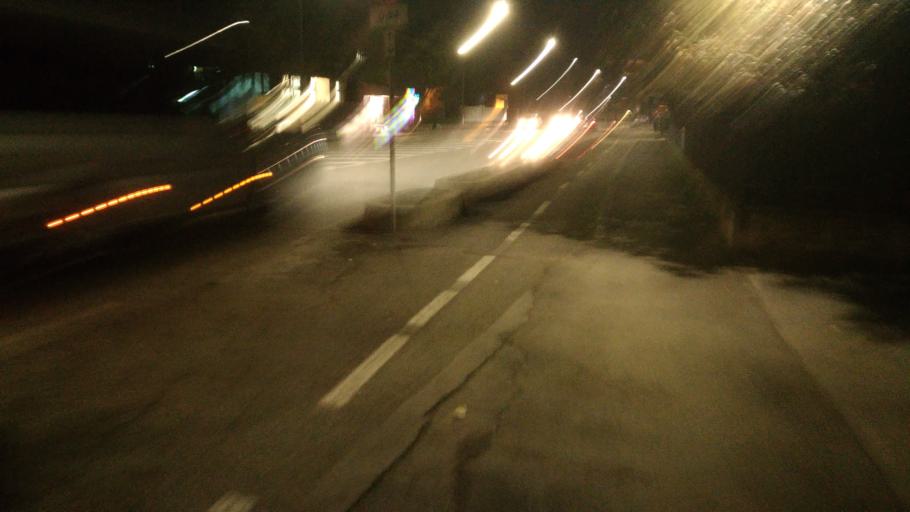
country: IT
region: Emilia-Romagna
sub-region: Provincia di Bologna
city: Trebbo
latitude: 44.5314
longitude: 11.3472
